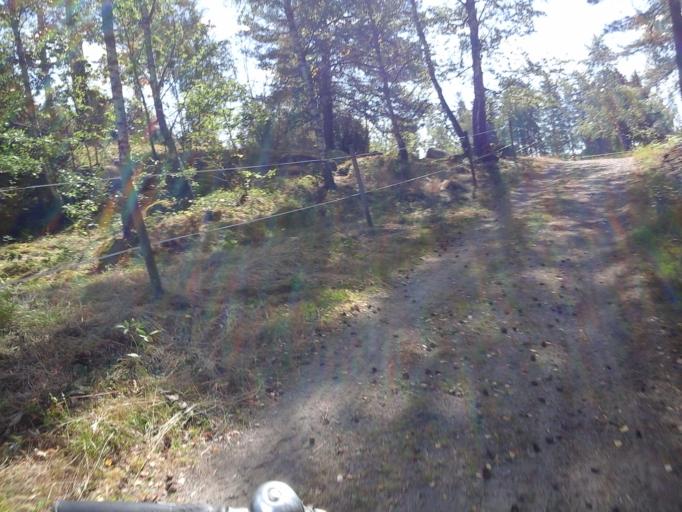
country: SE
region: Soedermanland
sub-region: Eskilstuna Kommun
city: Arla
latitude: 59.2452
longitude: 16.7736
